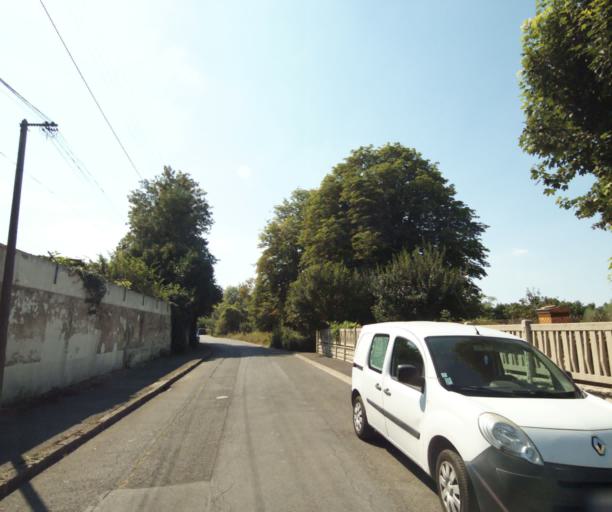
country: FR
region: Ile-de-France
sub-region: Departement de Seine-et-Marne
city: Pomponne
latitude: 48.8791
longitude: 2.6871
